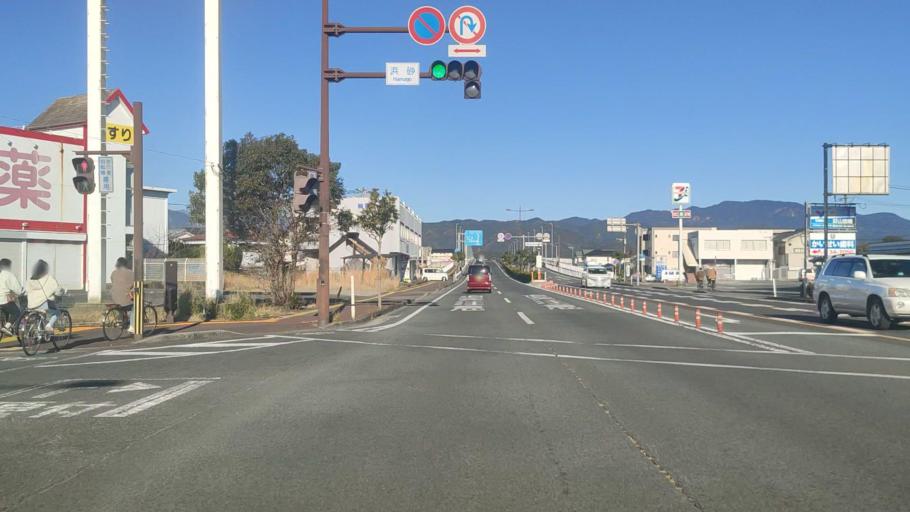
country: JP
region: Miyazaki
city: Nobeoka
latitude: 32.5795
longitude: 131.6824
